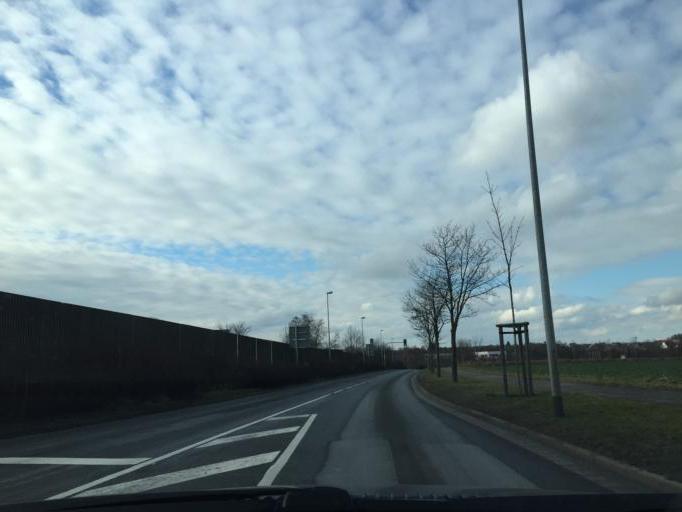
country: DE
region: Saxony
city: Radeberg
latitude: 51.1249
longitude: 13.9314
